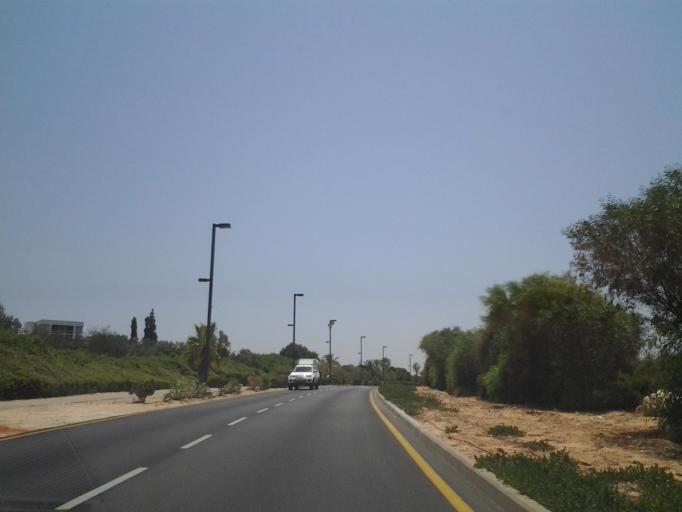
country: IL
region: Haifa
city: Qesarya
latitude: 32.5254
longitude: 34.9087
